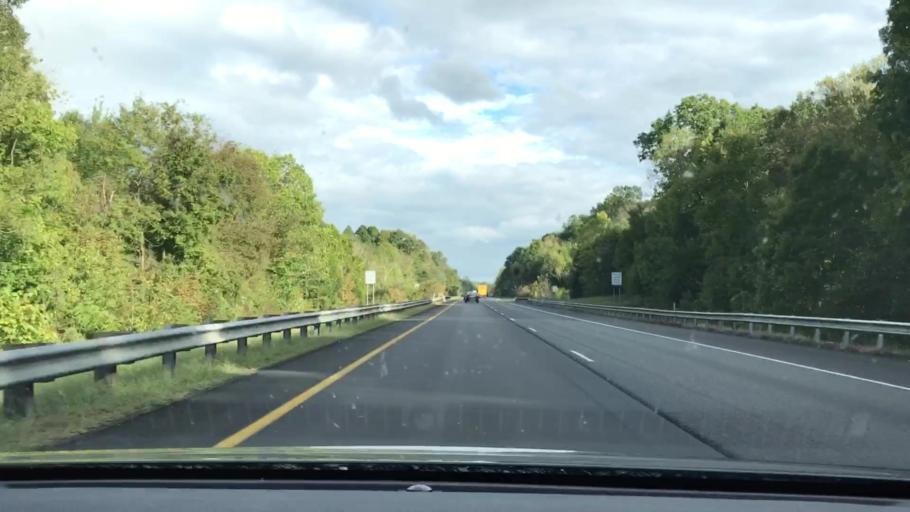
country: US
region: Tennessee
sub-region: Robertson County
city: Coopertown
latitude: 36.3663
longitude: -86.9648
